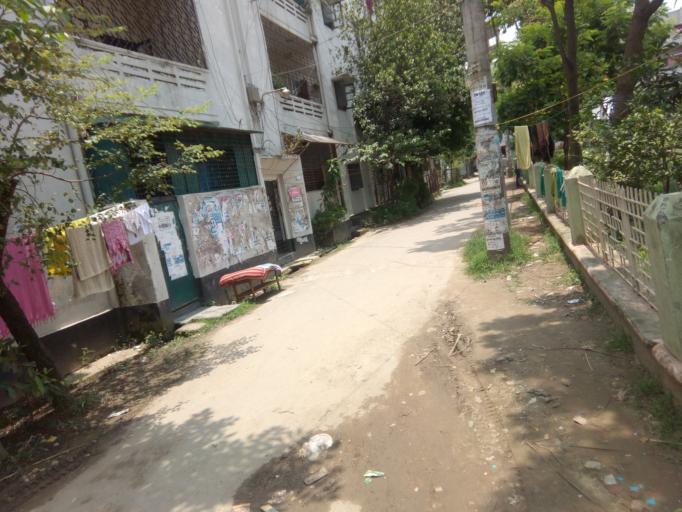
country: BD
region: Dhaka
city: Paltan
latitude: 23.7355
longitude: 90.4209
